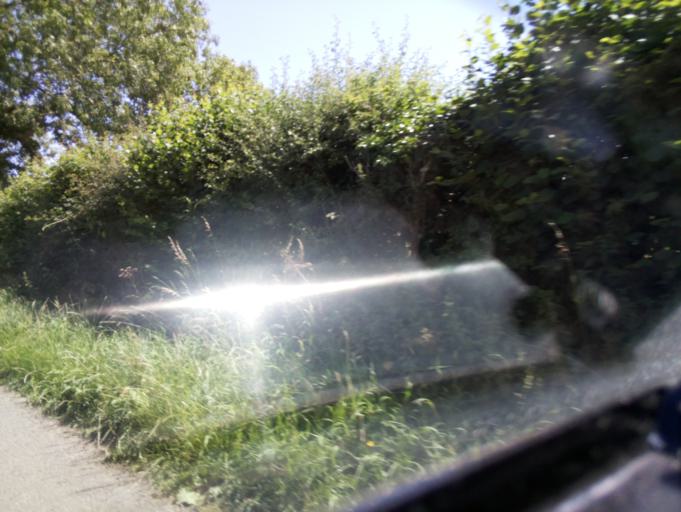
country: GB
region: England
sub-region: Wiltshire
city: Norton
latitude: 51.5171
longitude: -2.1867
